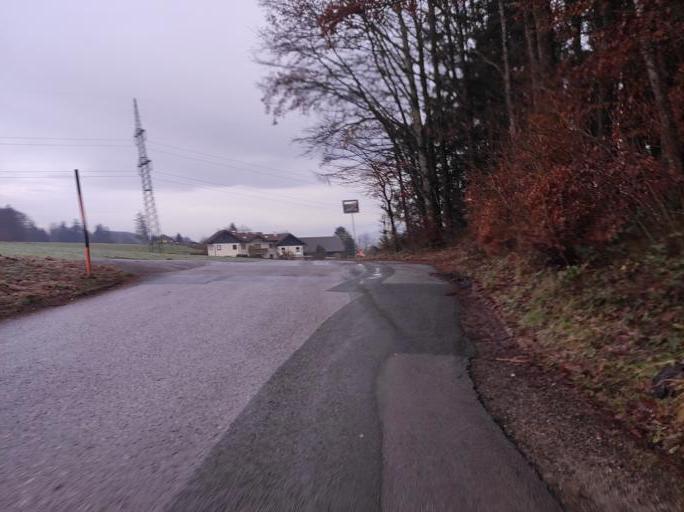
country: AT
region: Salzburg
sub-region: Politischer Bezirk Salzburg-Umgebung
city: Obertrum am See
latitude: 47.9152
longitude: 13.0689
